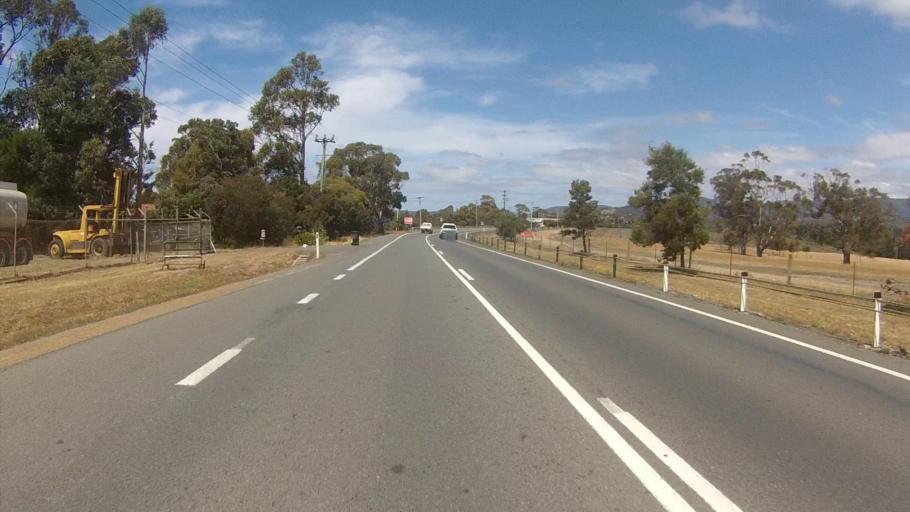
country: AU
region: Tasmania
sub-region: Kingborough
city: Margate
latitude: -43.0145
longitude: 147.2717
